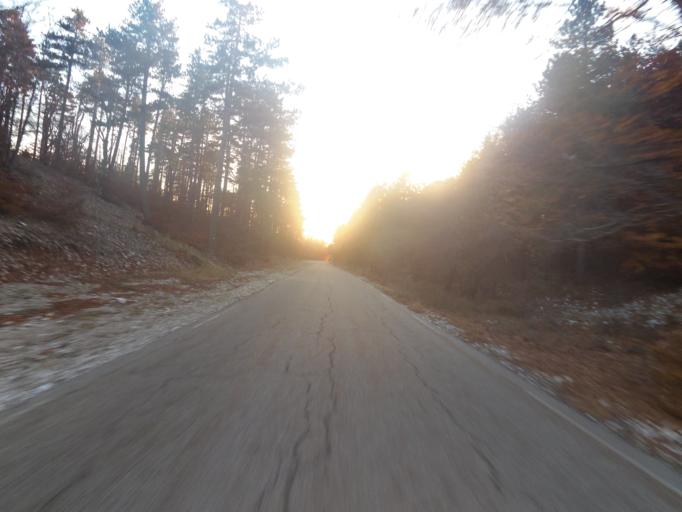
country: FR
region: Provence-Alpes-Cote d'Azur
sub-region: Departement du Vaucluse
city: Sault
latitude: 44.1371
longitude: 5.3092
